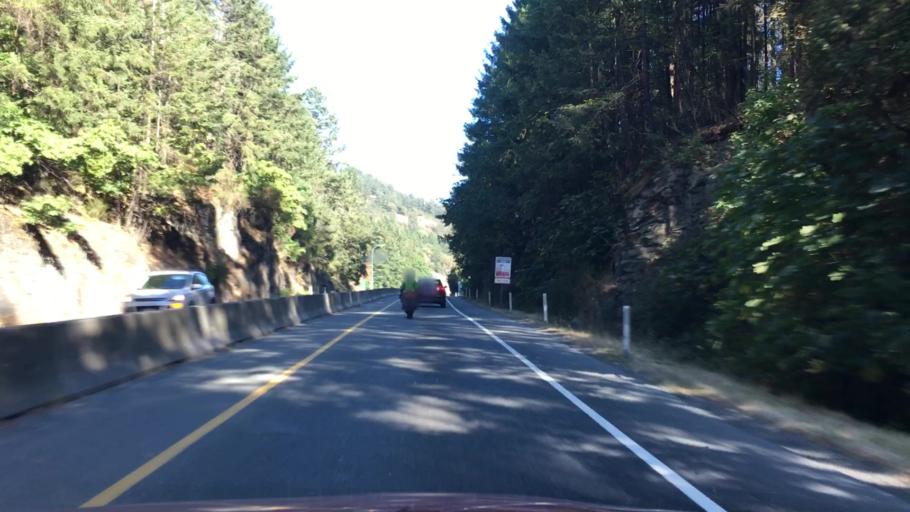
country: CA
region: British Columbia
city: Langford
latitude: 48.4614
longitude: -123.5470
